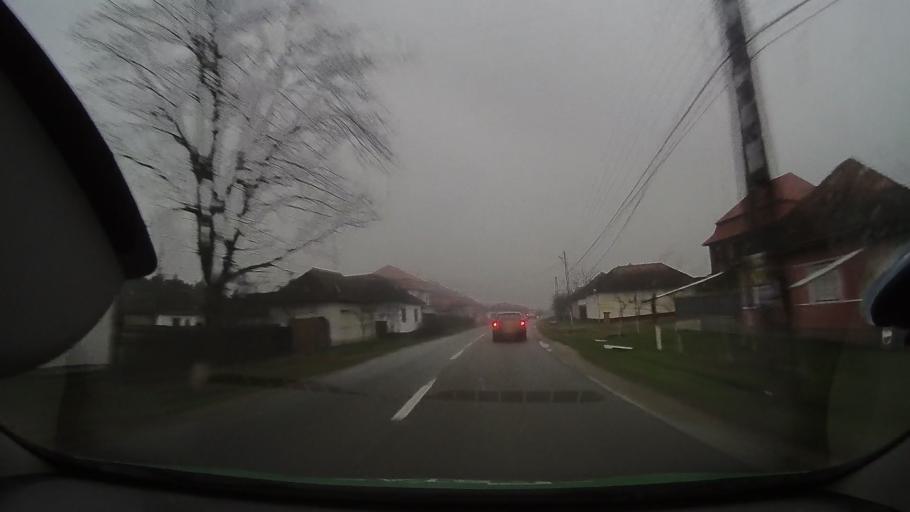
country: RO
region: Arad
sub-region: Comuna Craiova
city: Craiova
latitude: 46.5751
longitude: 21.9739
